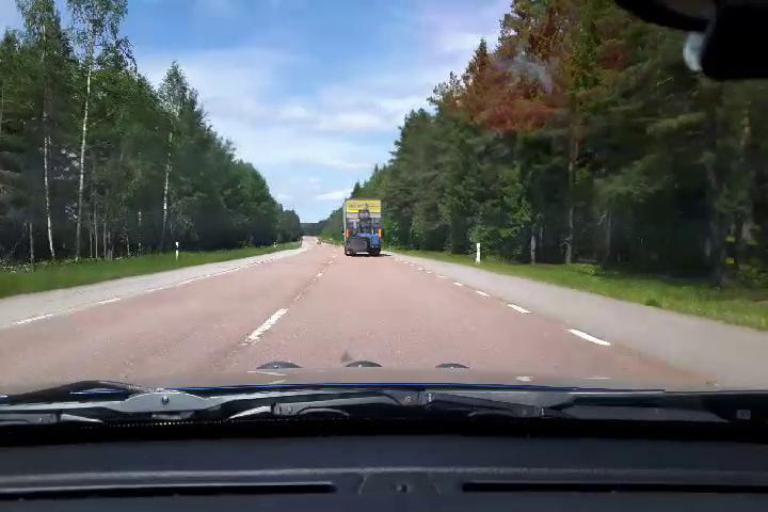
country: SE
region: Uppsala
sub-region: Osthammars Kommun
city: Bjorklinge
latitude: 60.1325
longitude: 17.5089
